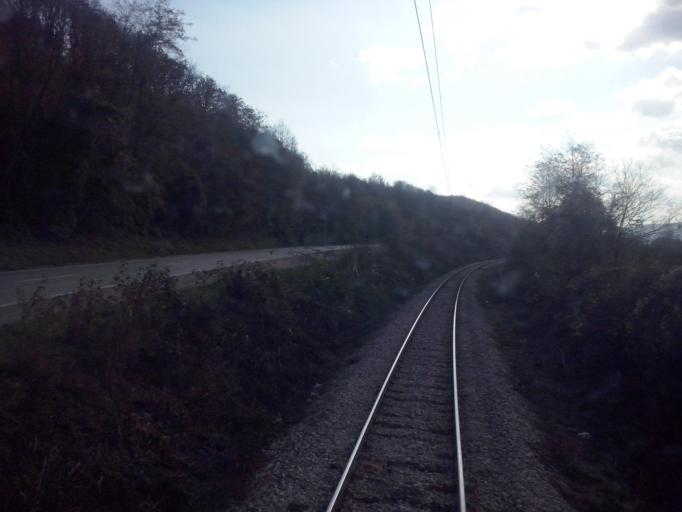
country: RS
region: Central Serbia
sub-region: Zlatiborski Okrug
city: Pozega
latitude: 43.8888
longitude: 19.9987
